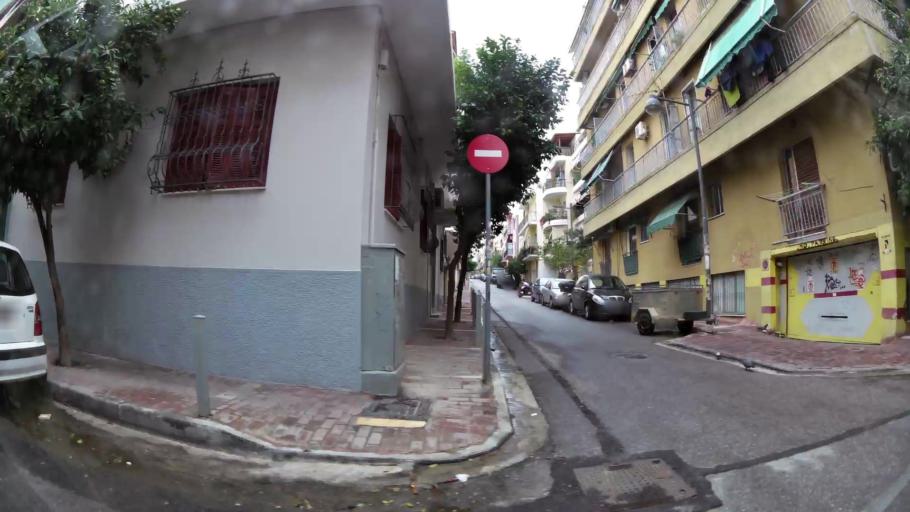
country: GR
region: Attica
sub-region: Nomarchia Athinas
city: Kaisariani
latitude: 37.9617
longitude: 23.7601
